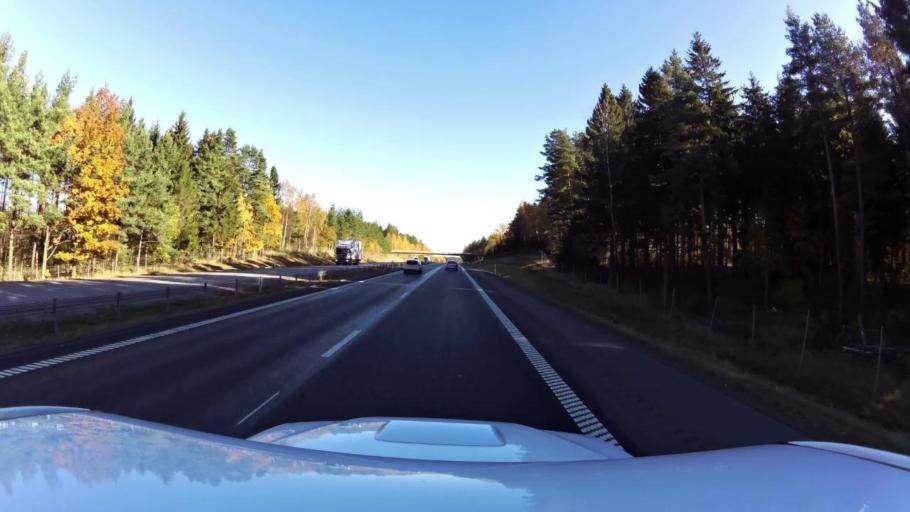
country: SE
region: OEstergoetland
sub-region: Mjolby Kommun
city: Mantorp
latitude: 58.3805
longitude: 15.3501
